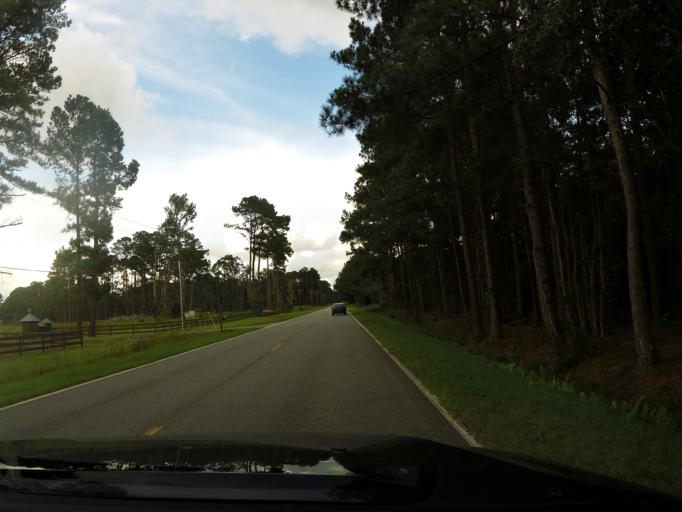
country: US
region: Georgia
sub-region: Liberty County
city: Midway
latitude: 31.8514
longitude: -81.4223
